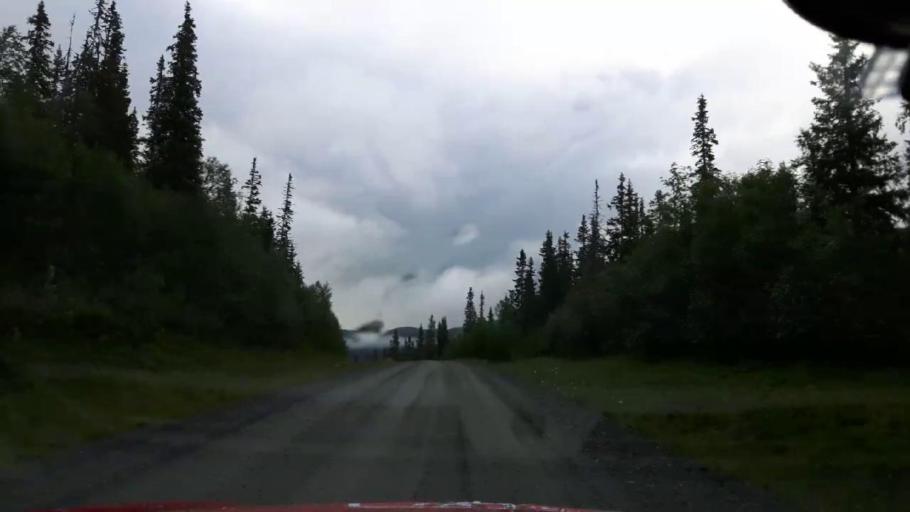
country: NO
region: Nordland
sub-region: Hattfjelldal
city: Hattfjelldal
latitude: 64.8854
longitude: 14.7647
